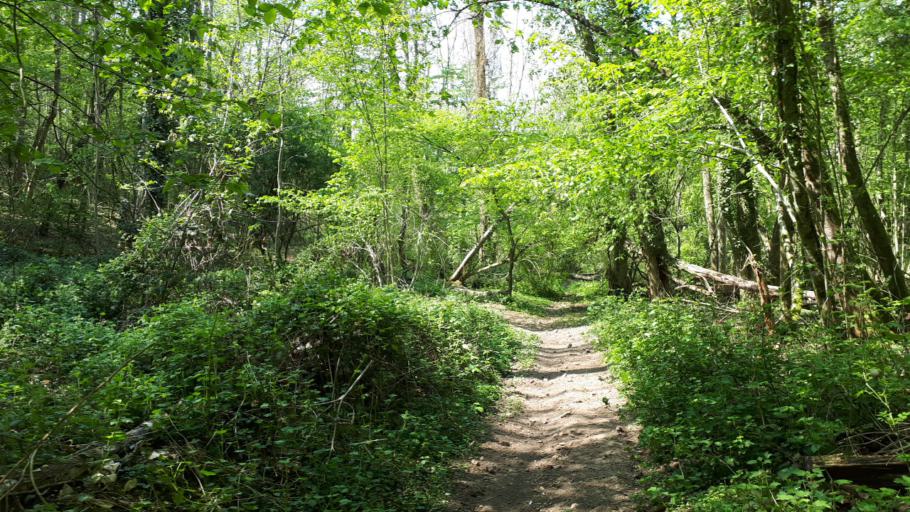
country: FR
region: Centre
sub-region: Departement du Loir-et-Cher
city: Villiers-sur-Loir
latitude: 47.8188
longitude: 0.9723
